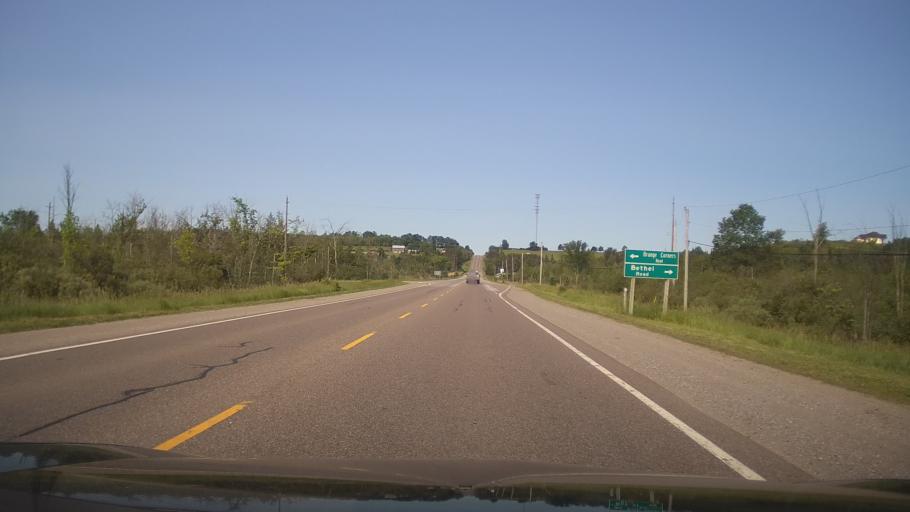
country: CA
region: Ontario
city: Omemee
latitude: 44.3199
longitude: -78.4738
